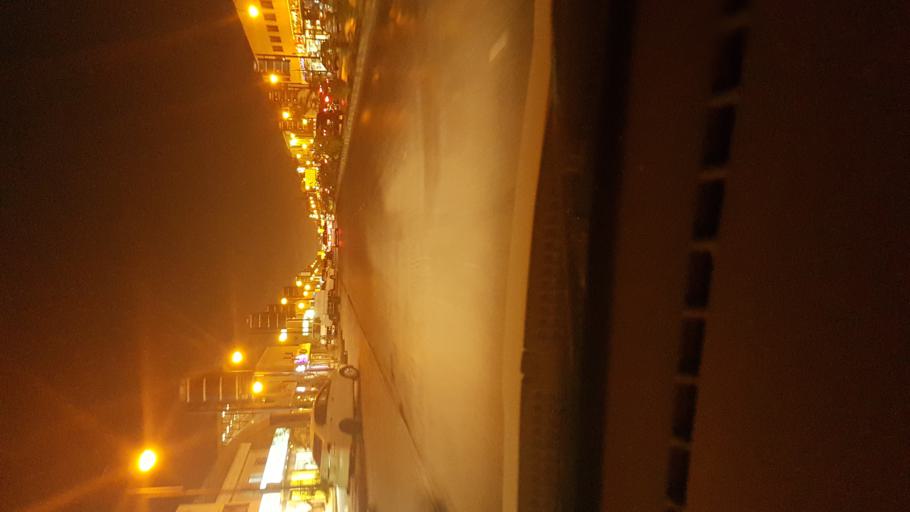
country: SA
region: Ar Riyad
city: Riyadh
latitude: 24.6909
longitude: 46.6900
